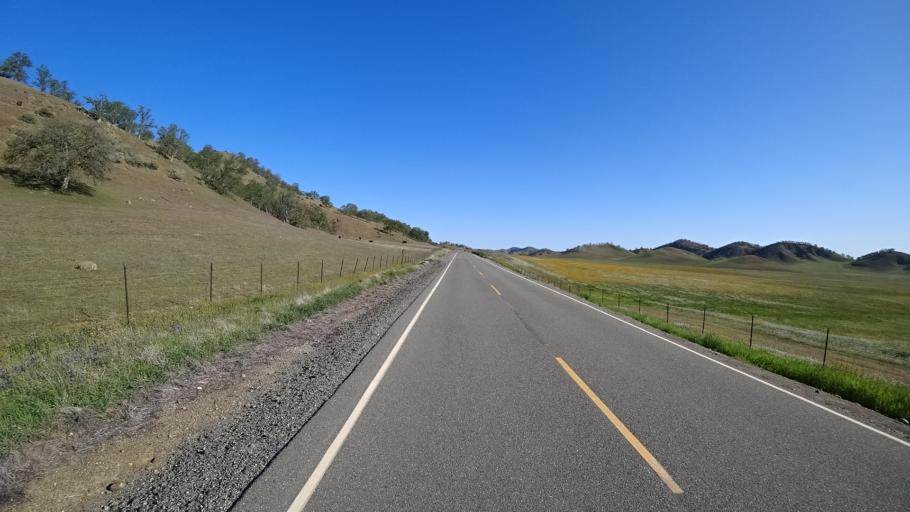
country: US
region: California
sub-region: Tehama County
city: Rancho Tehama Reserve
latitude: 39.7578
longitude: -122.5247
